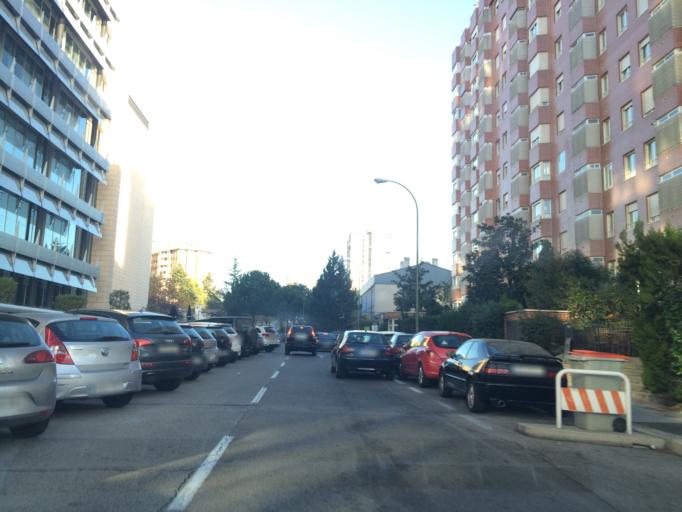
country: ES
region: Madrid
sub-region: Provincia de Madrid
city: Pinar de Chamartin
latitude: 40.4757
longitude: -3.6720
